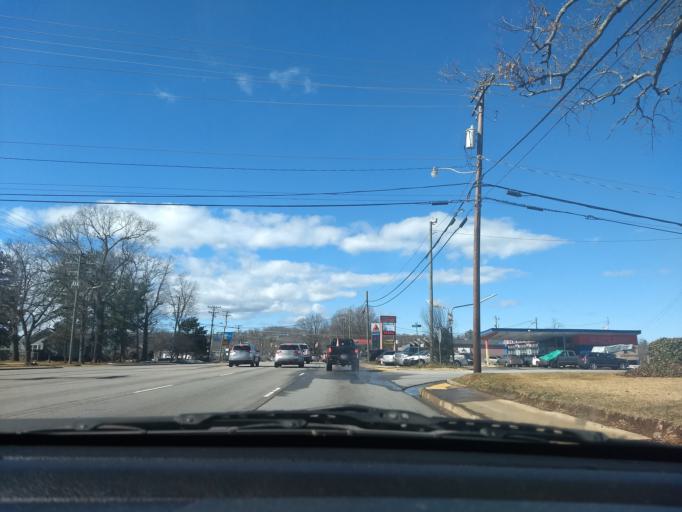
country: US
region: South Carolina
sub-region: Greenville County
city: Wade Hampton
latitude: 34.8871
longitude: -82.3710
